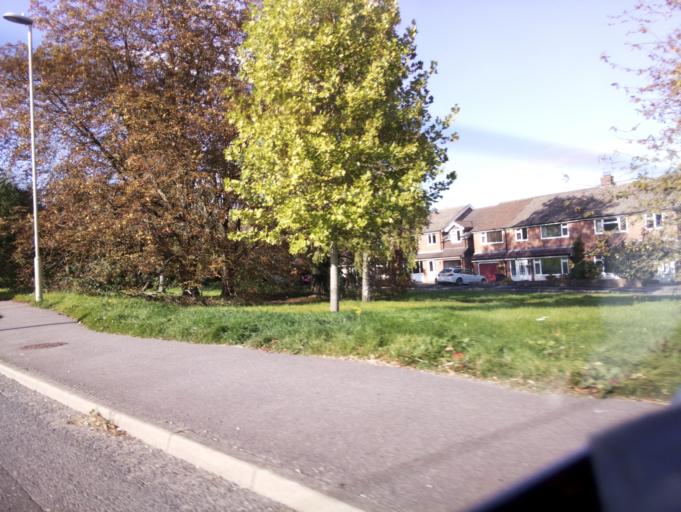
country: GB
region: England
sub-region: Hampshire
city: Alton
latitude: 51.1434
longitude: -0.9891
